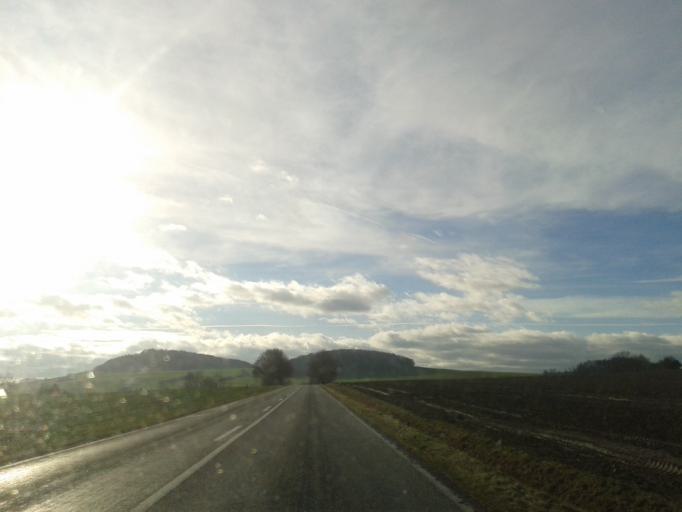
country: DE
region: Saxony
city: Eibau
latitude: 50.9810
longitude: 14.6993
